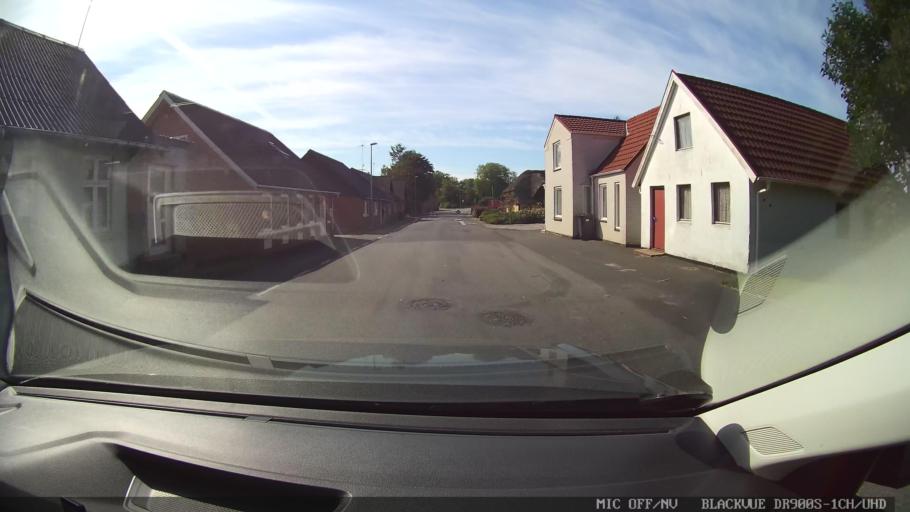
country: DK
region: North Denmark
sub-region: Mariagerfjord Kommune
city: Hobro
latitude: 56.5392
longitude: 9.8254
